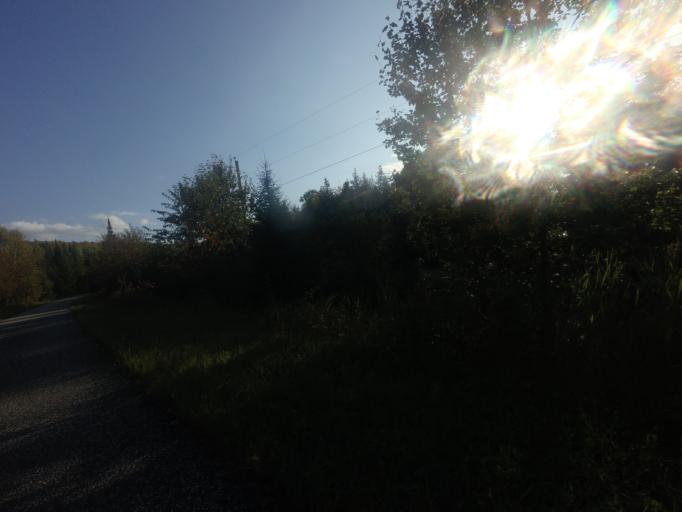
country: CA
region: Quebec
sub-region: Laurentides
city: Riviere-Rouge
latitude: 46.4199
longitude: -74.9442
